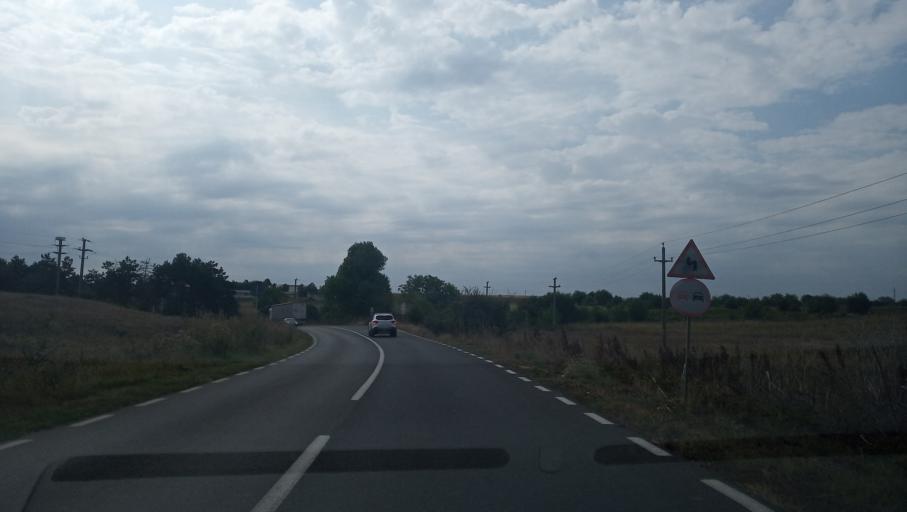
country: RO
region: Constanta
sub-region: Comuna Limanu
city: Limanu
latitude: 43.8231
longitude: 28.5256
